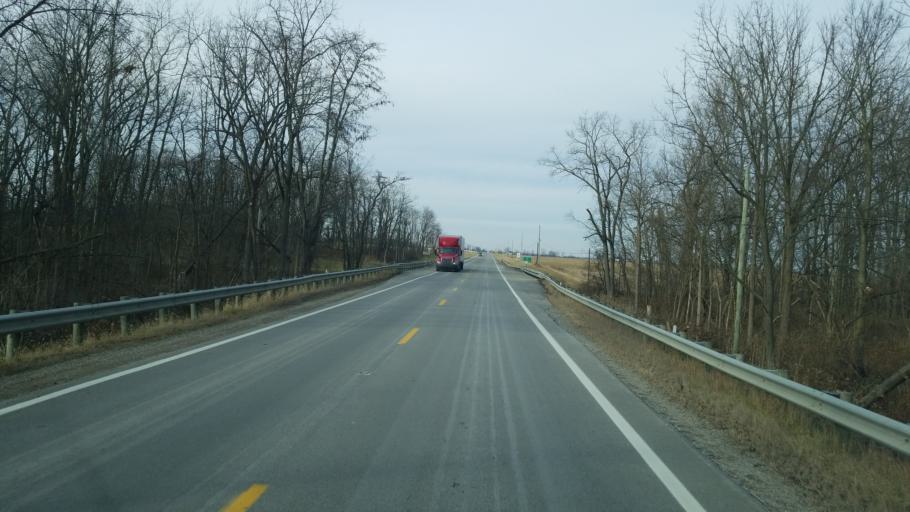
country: US
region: Ohio
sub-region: Hardin County
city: Kenton
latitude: 40.5035
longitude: -83.4967
